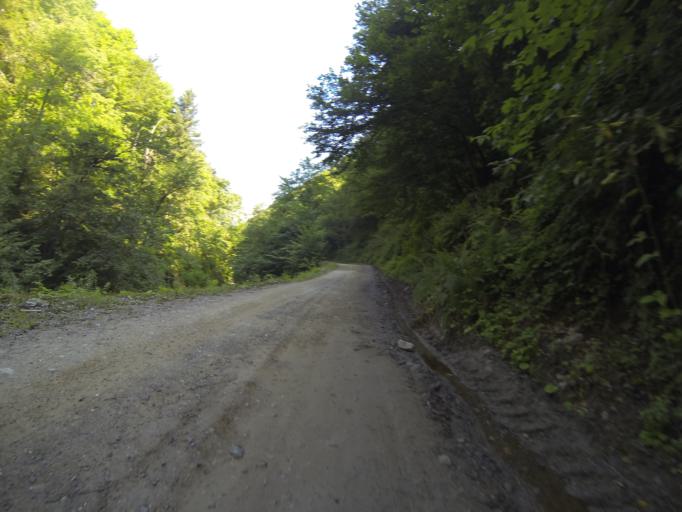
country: RO
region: Valcea
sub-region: Comuna Costesti
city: Bistrita
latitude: 45.2217
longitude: 24.0039
